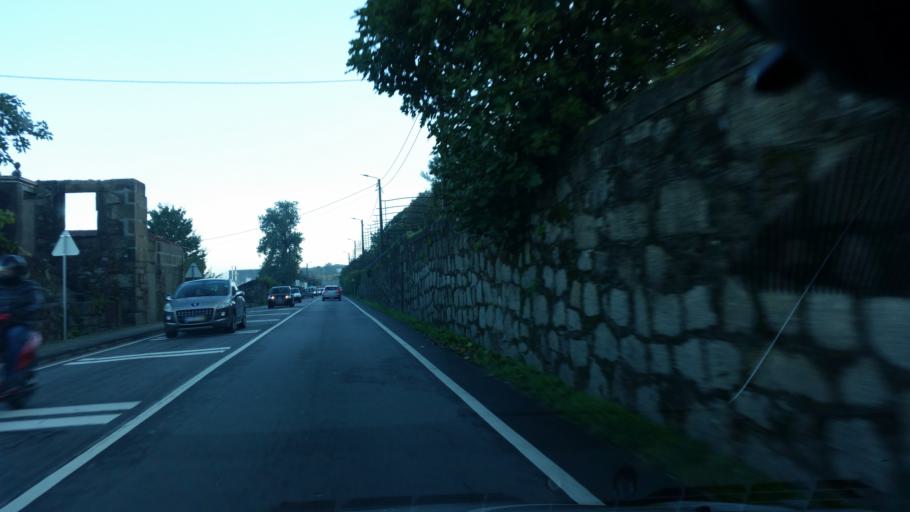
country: PT
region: Porto
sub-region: Santo Tirso
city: Sao Miguel do Couto
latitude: 41.3540
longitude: -8.4491
